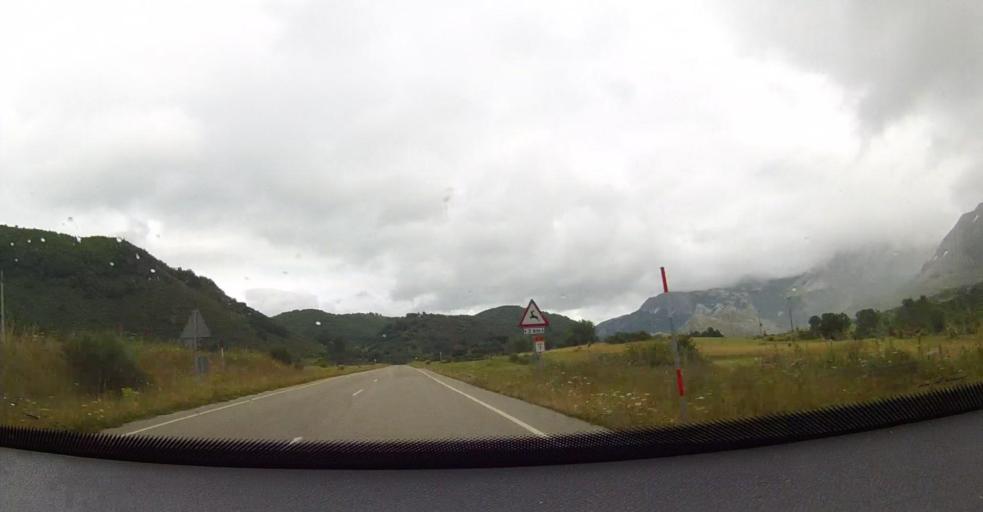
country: ES
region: Castille and Leon
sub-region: Provincia de Leon
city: Acebedo
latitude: 43.0394
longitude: -5.0868
